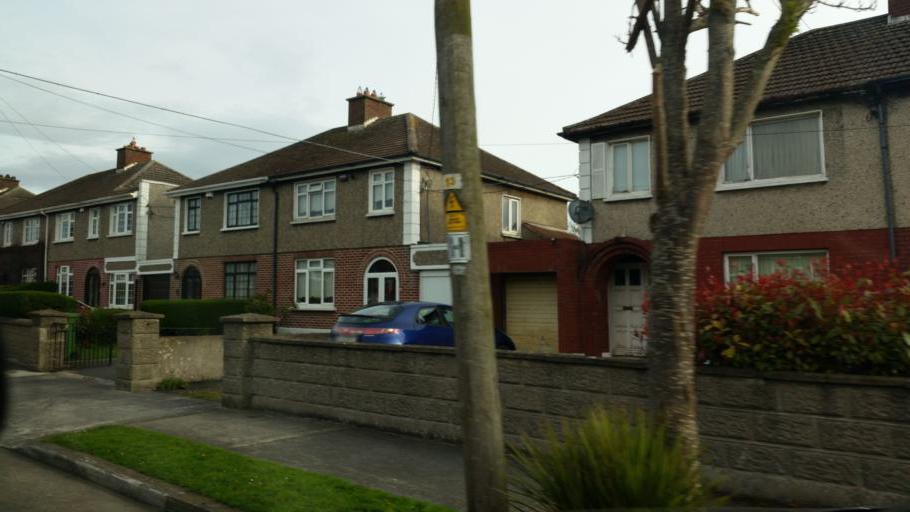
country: IE
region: Leinster
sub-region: Dublin City
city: Finglas
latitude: 53.3962
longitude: -6.2852
